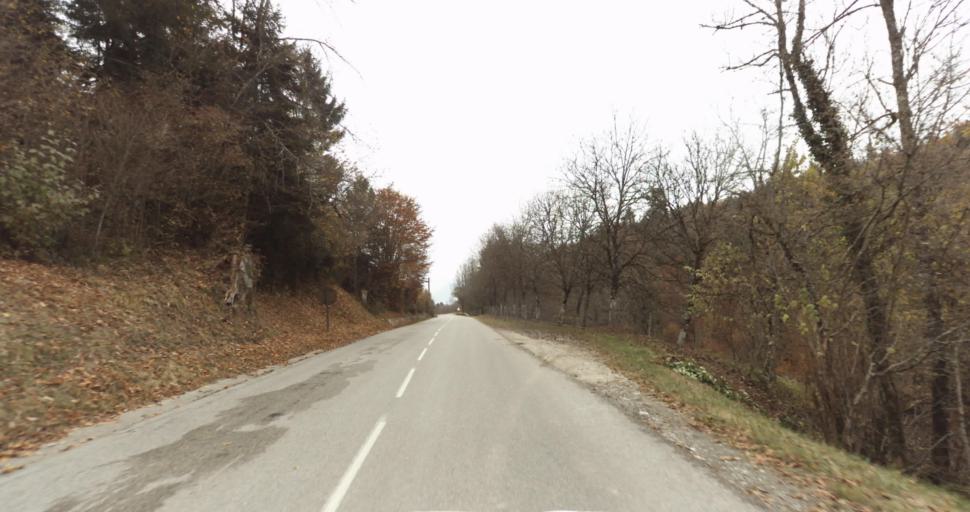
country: FR
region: Rhone-Alpes
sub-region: Departement de la Haute-Savoie
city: Saint-Jorioz
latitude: 45.8054
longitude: 6.1441
